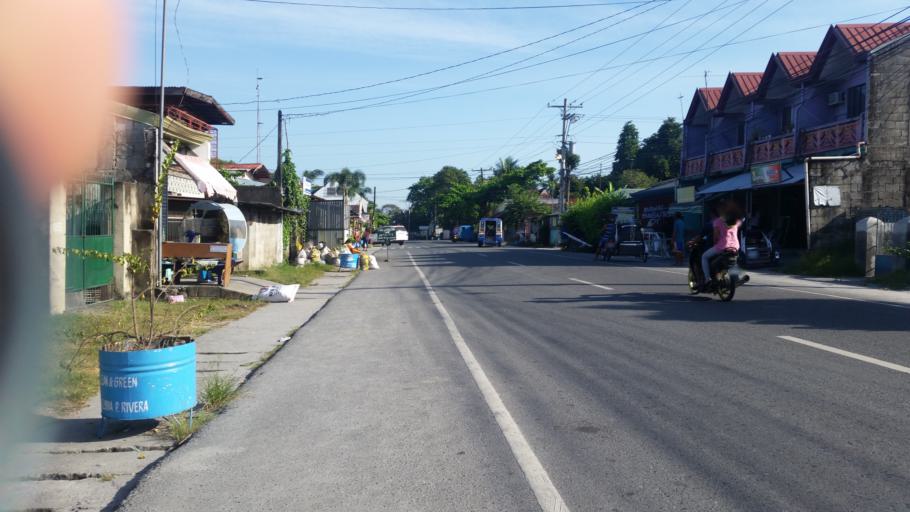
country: PH
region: Central Luzon
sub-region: Province of Pampanga
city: Mabalacat City
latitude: 15.2763
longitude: 120.5677
